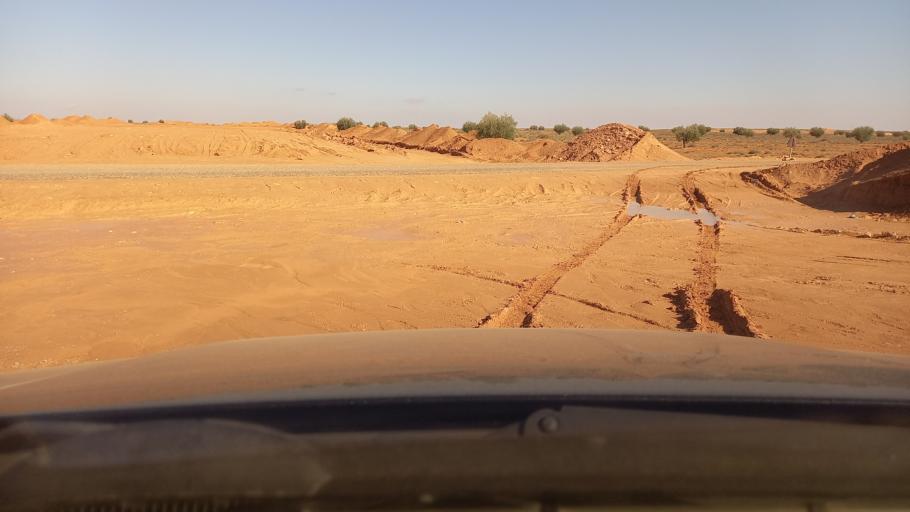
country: TN
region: Madanin
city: Medenine
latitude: 33.1777
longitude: 10.5290
